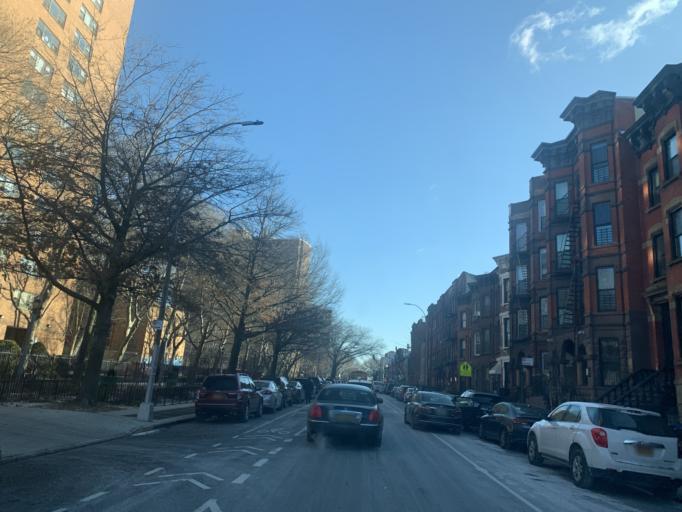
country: US
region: New York
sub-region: Kings County
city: Brooklyn
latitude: 40.6887
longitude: -73.9622
